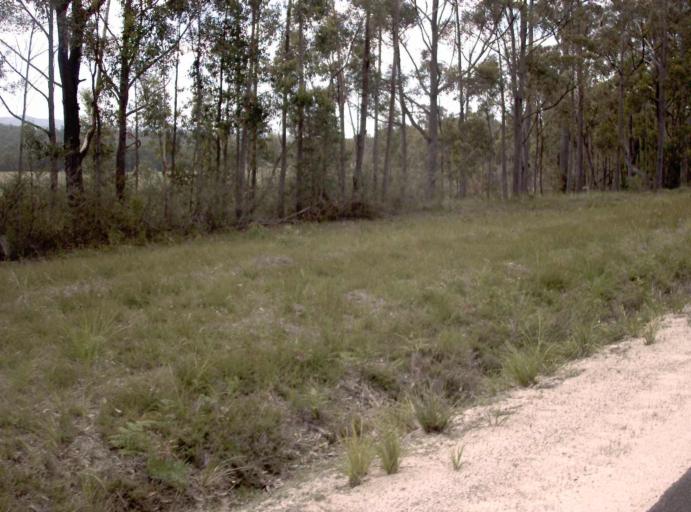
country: AU
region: New South Wales
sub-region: Bega Valley
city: Eden
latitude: -37.5423
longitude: 149.4604
